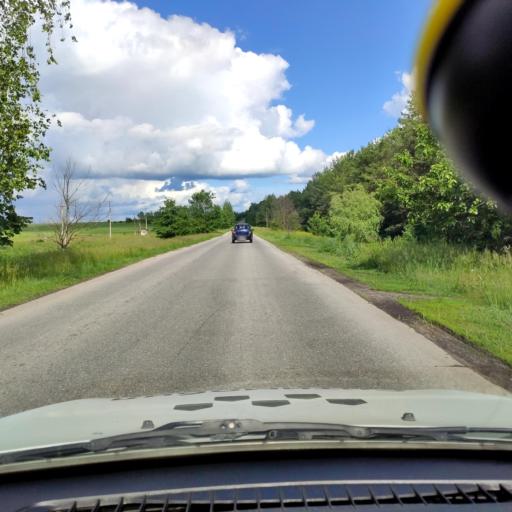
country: RU
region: Samara
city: Povolzhskiy
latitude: 53.6478
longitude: 49.7446
